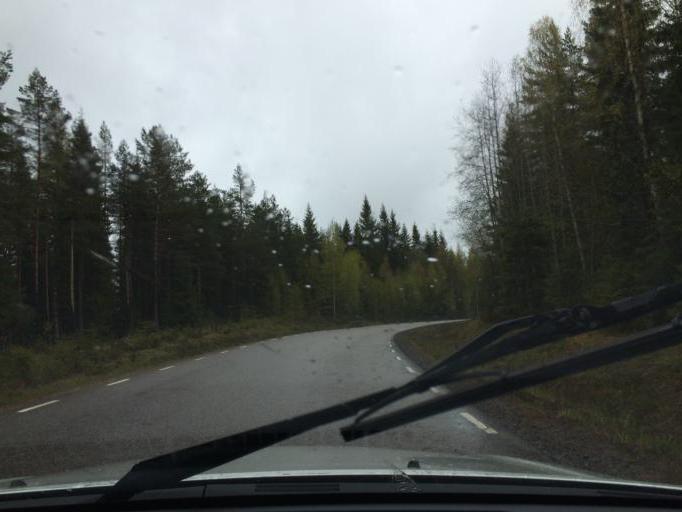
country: SE
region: Dalarna
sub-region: Ludvika Kommun
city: Abborrberget
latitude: 60.0660
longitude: 14.8274
